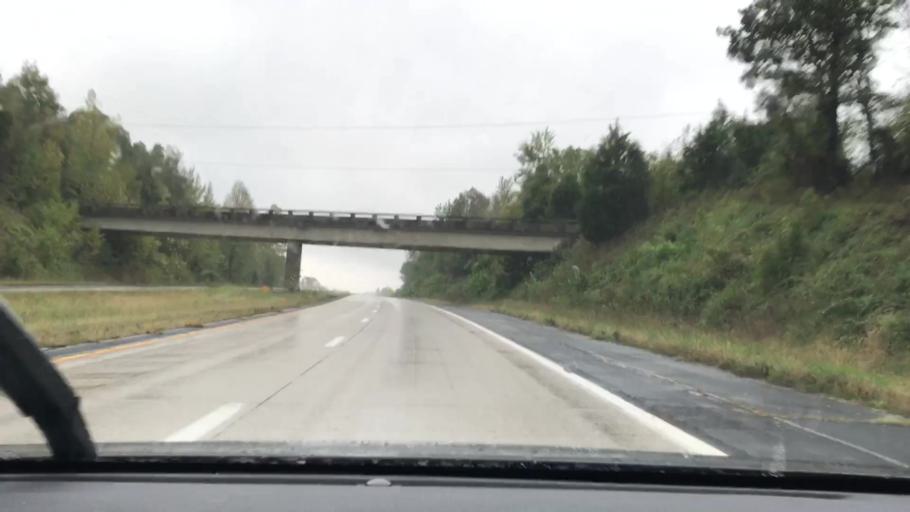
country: US
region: Kentucky
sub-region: Hopkins County
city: Nortonville
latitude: 37.1432
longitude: -87.4641
